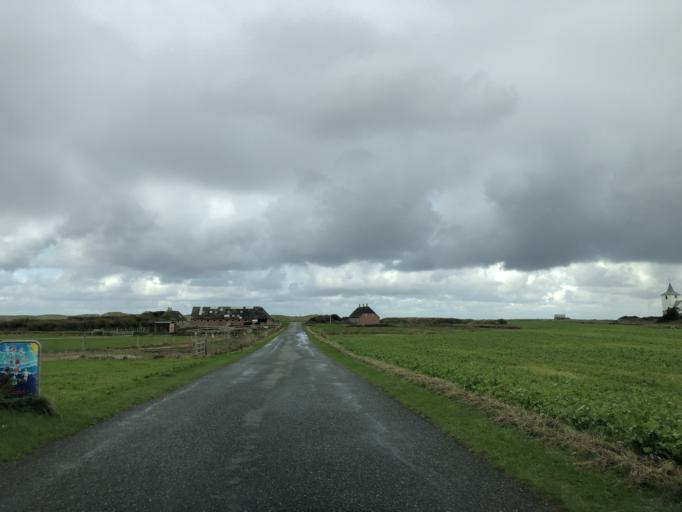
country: DK
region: Central Jutland
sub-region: Lemvig Kommune
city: Harboore
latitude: 56.4737
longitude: 8.1364
